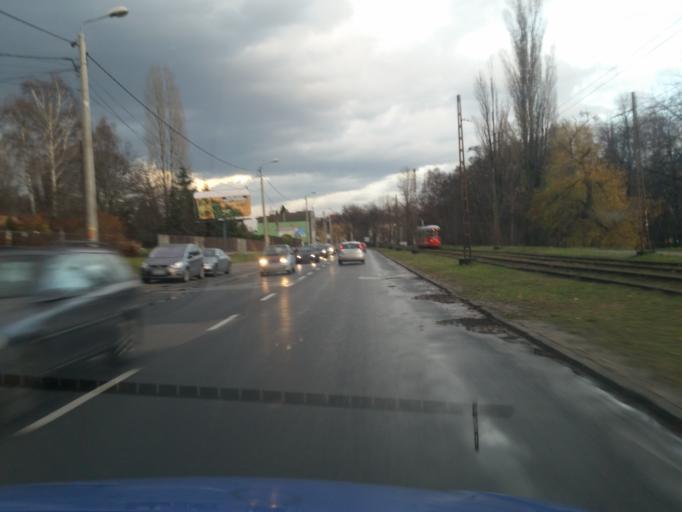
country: PL
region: Silesian Voivodeship
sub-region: Myslowice
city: Myslowice
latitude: 50.2694
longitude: 19.1653
